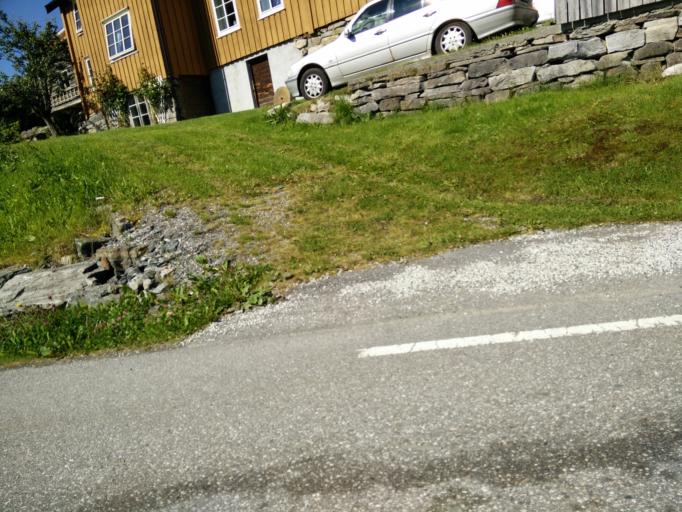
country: NO
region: More og Romsdal
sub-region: Kristiansund
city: Rensvik
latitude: 63.0206
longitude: 7.9469
